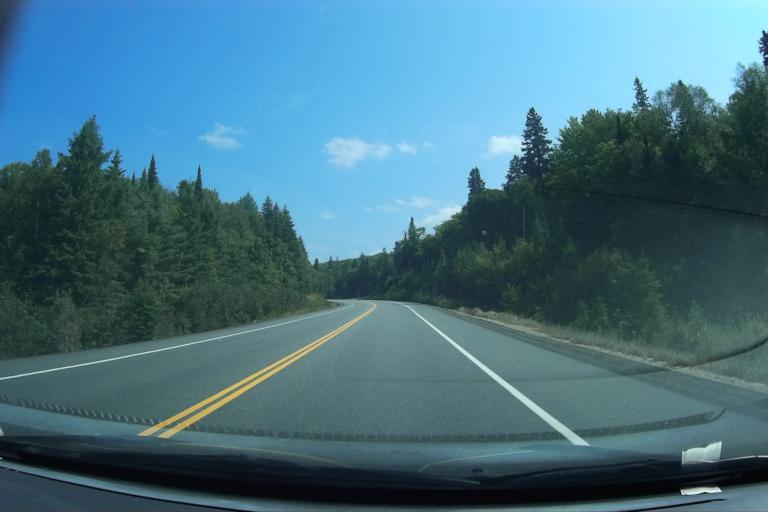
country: CA
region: Ontario
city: Huntsville
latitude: 45.5427
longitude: -78.6650
